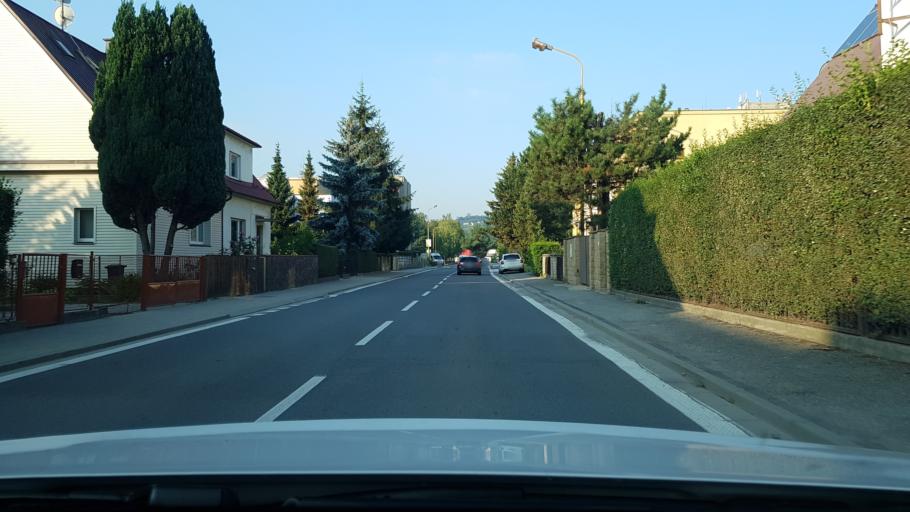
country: SK
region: Trenciansky
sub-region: Okres Povazska Bystrica
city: Povazska Bystrica
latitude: 49.1227
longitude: 18.4281
